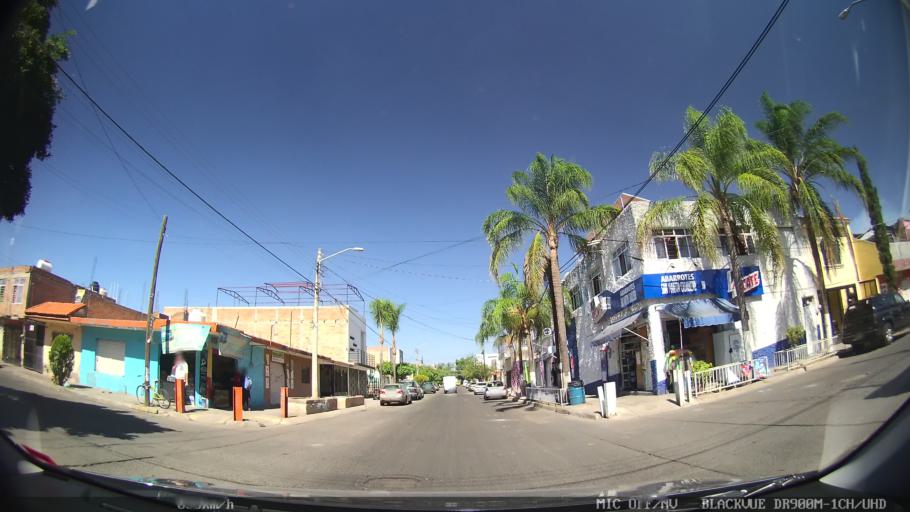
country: MX
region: Jalisco
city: Tlaquepaque
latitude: 20.6517
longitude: -103.2860
